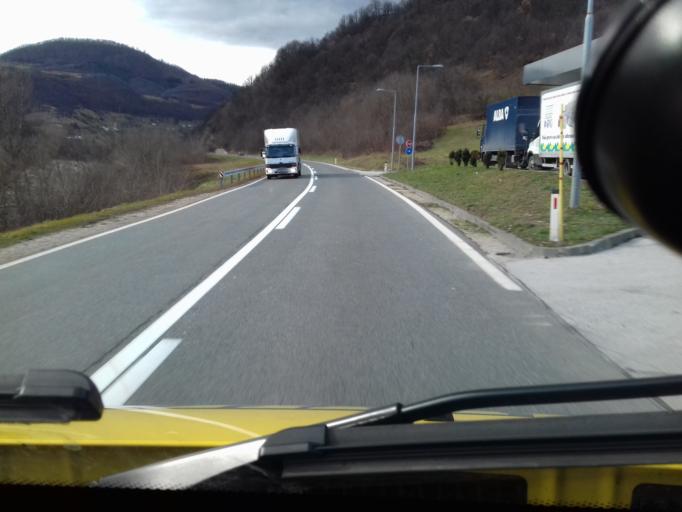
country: BA
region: Federation of Bosnia and Herzegovina
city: Kacuni
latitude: 44.1303
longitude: 17.9675
